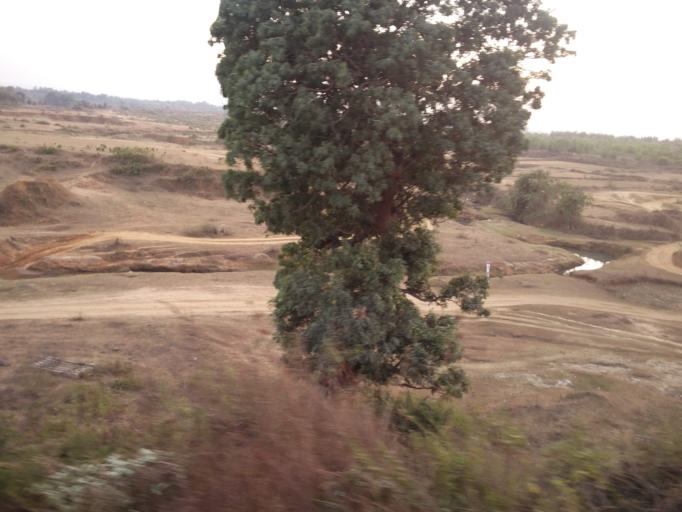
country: IN
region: Jharkhand
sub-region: Giridih
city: Hesla
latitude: 24.0797
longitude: 85.9723
